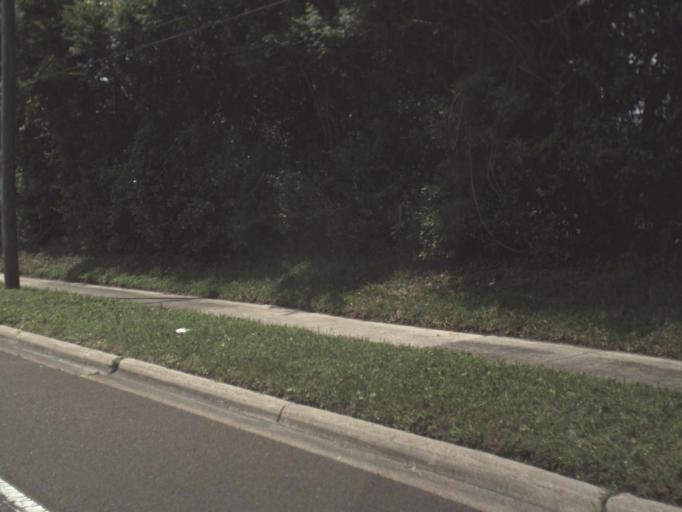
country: US
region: Florida
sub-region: Duval County
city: Jacksonville
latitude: 30.2993
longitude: -81.6493
